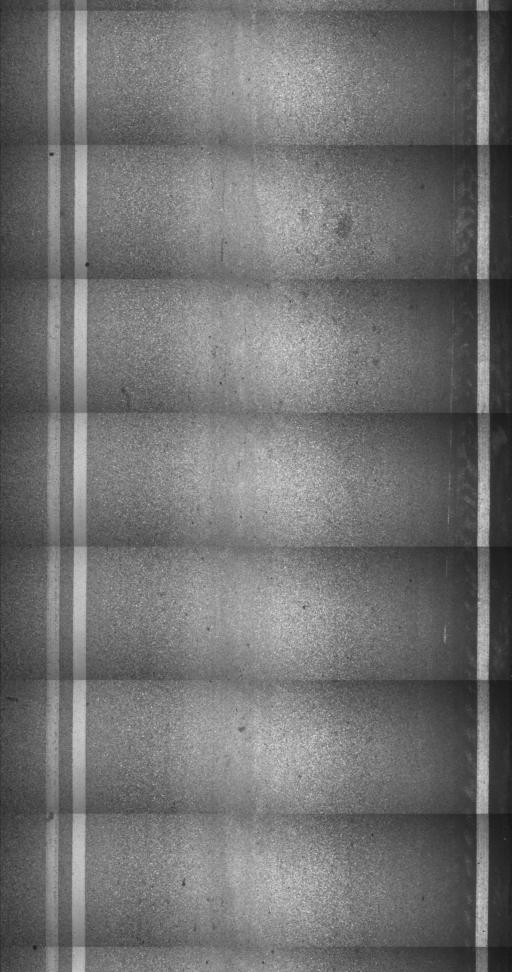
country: US
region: Vermont
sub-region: Franklin County
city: Enosburg Falls
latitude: 44.9046
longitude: -72.9477
